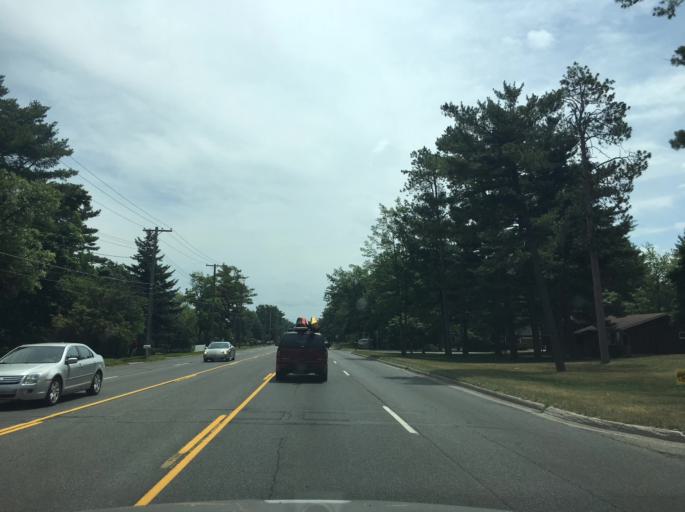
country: US
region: Michigan
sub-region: Grand Traverse County
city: Traverse City
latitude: 44.7540
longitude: -85.5708
